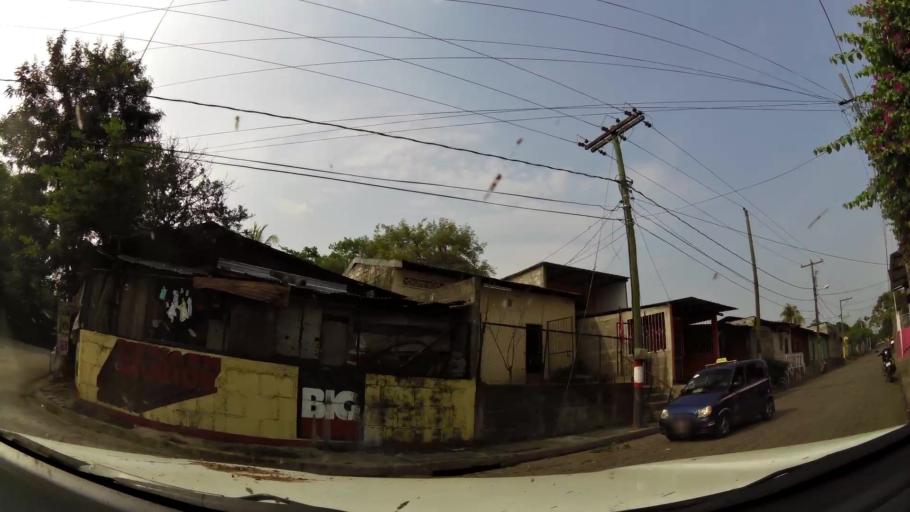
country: NI
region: Masaya
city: Masaya
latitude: 11.9704
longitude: -86.0972
